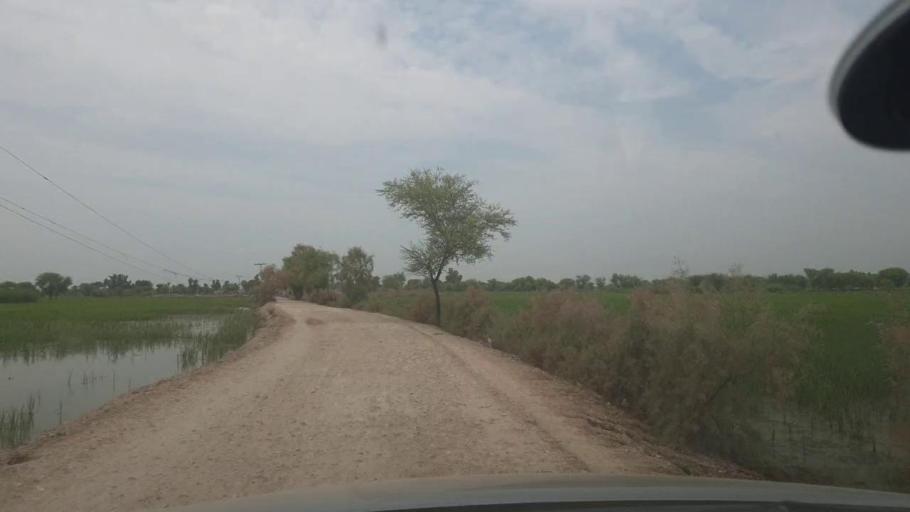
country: PK
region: Balochistan
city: Mehrabpur
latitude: 28.0595
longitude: 68.1399
